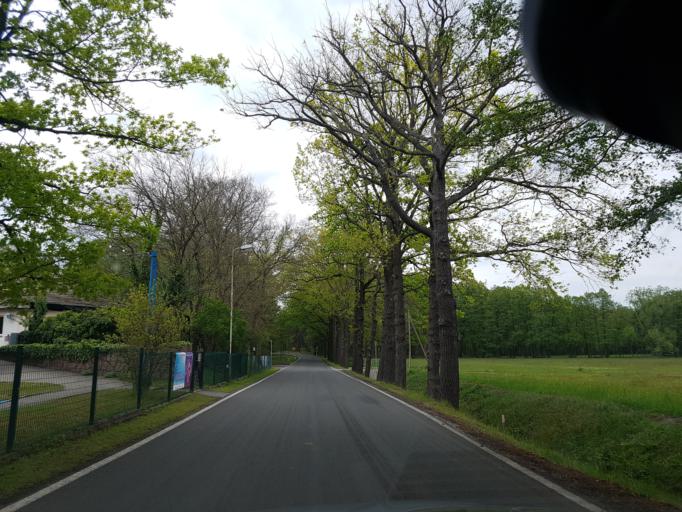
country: DE
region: Brandenburg
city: Crinitz
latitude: 51.7453
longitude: 13.7561
